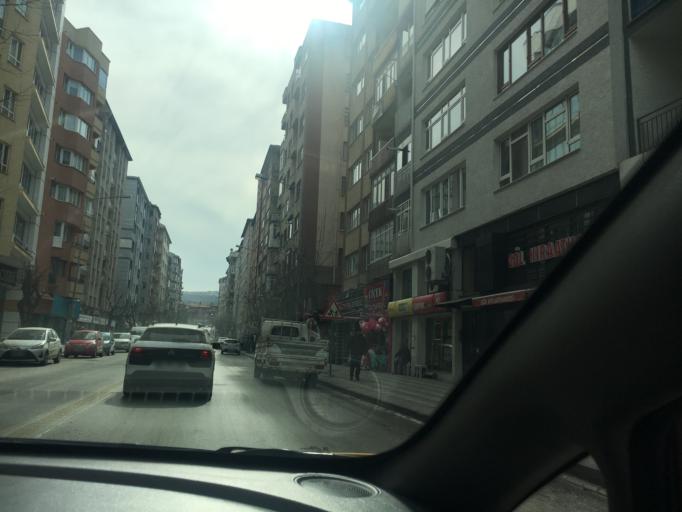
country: TR
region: Eskisehir
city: Eskisehir
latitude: 39.7679
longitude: 30.5185
